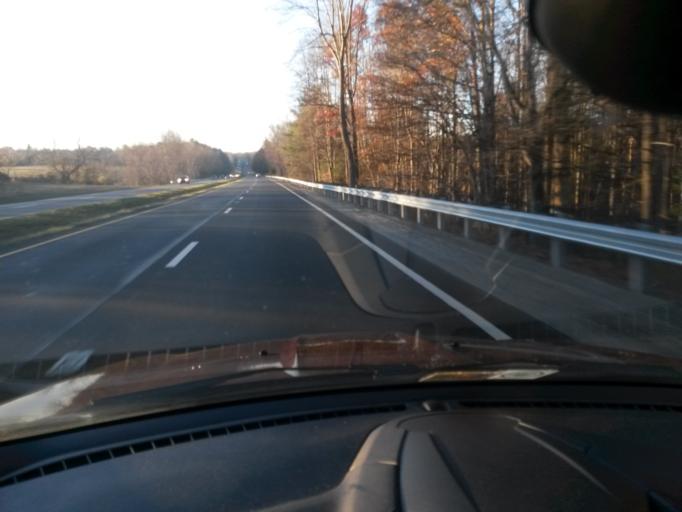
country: US
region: Virginia
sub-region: Franklin County
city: Henry Fork
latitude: 36.9795
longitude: -79.8722
